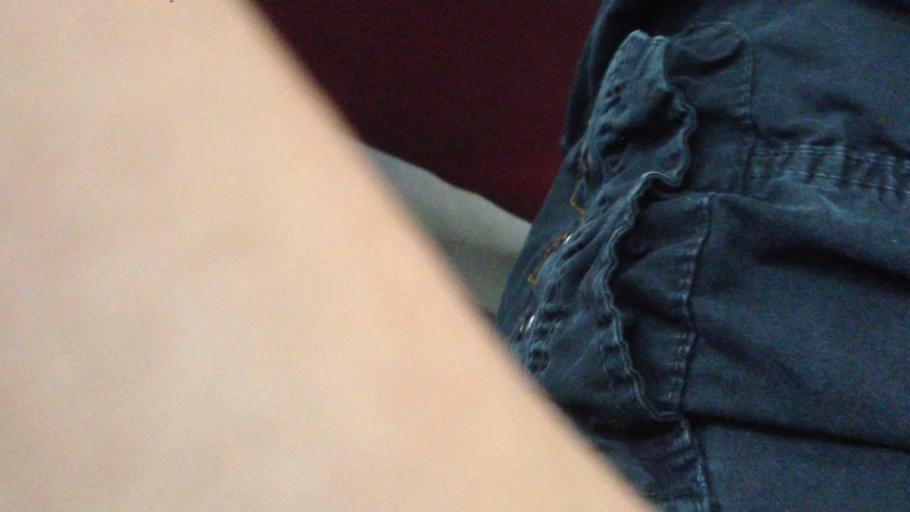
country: US
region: New York
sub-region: Dutchess County
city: Red Hook
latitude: 41.9871
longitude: -73.9142
